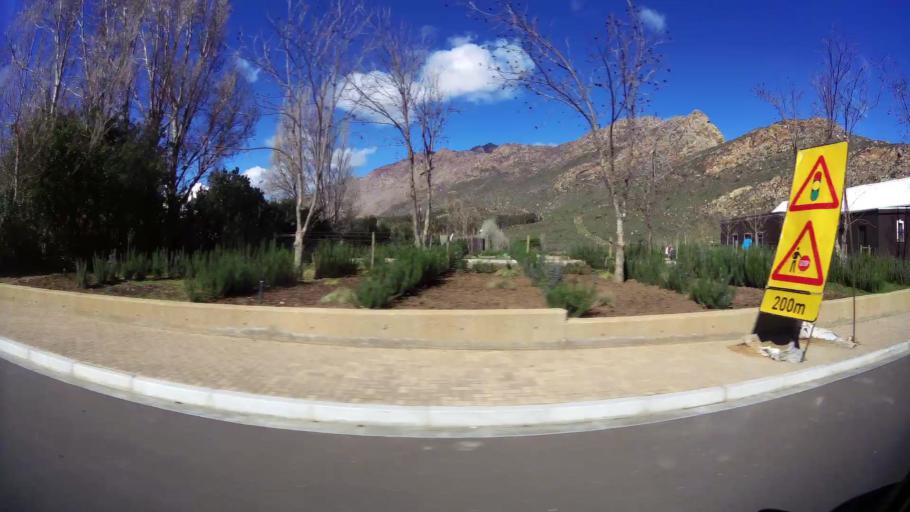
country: ZA
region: Western Cape
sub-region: Cape Winelands District Municipality
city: Ashton
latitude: -33.7910
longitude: 20.1115
